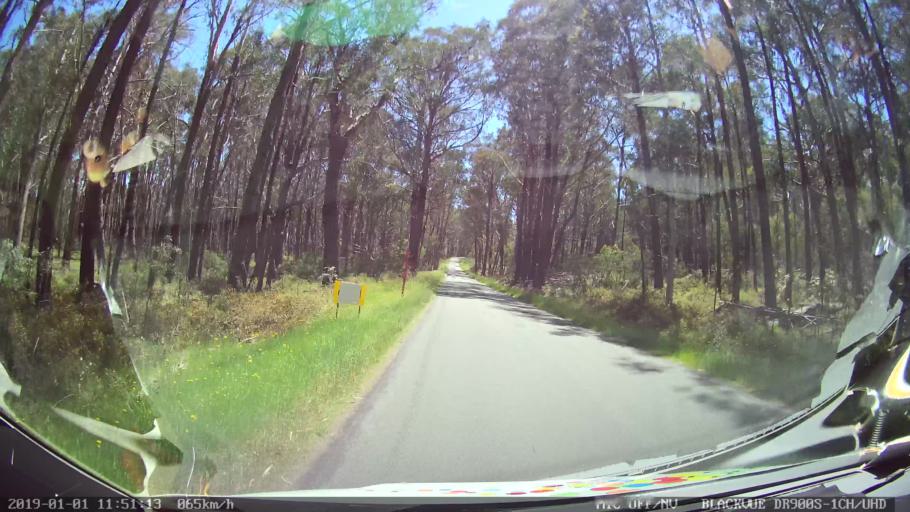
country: AU
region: New South Wales
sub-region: Snowy River
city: Jindabyne
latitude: -35.8870
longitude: 148.4283
